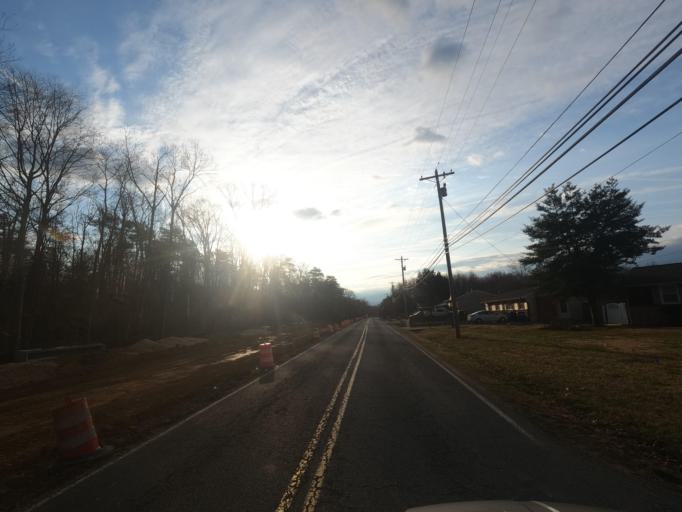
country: US
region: Maryland
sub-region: Charles County
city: Bryans Road
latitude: 38.6319
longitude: -77.0770
